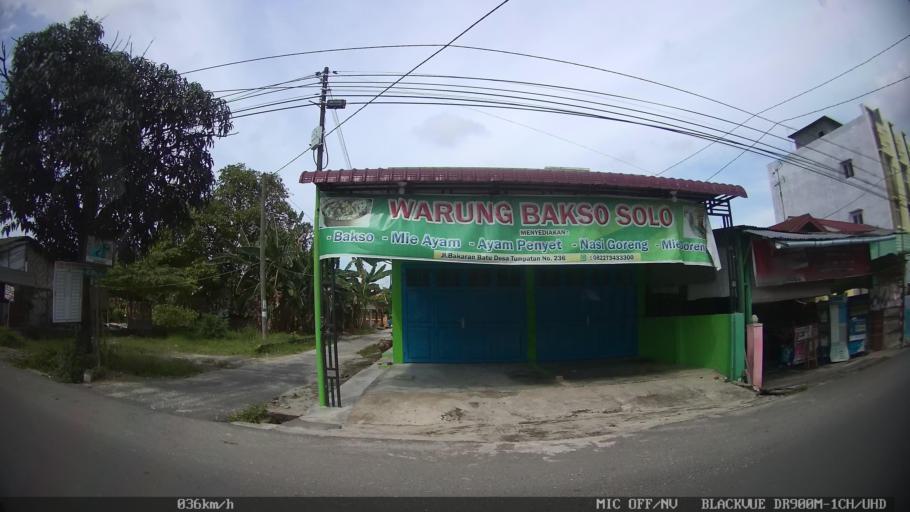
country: ID
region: North Sumatra
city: Percut
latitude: 3.5762
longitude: 98.8669
